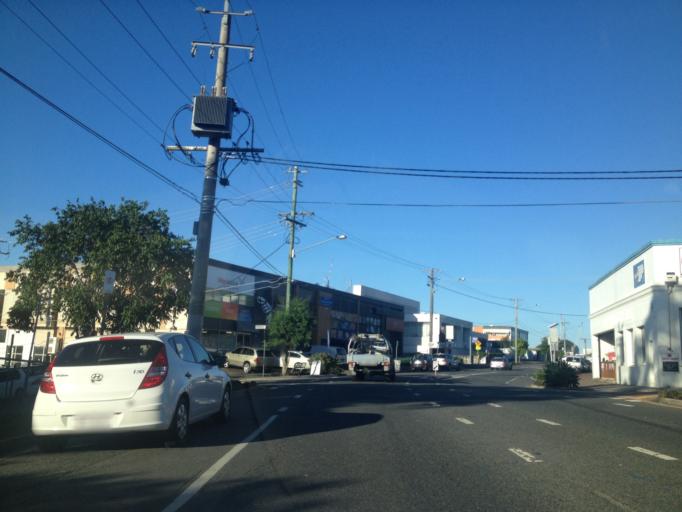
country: AU
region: Queensland
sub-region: Brisbane
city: Milton
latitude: -27.4806
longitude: 153.0083
